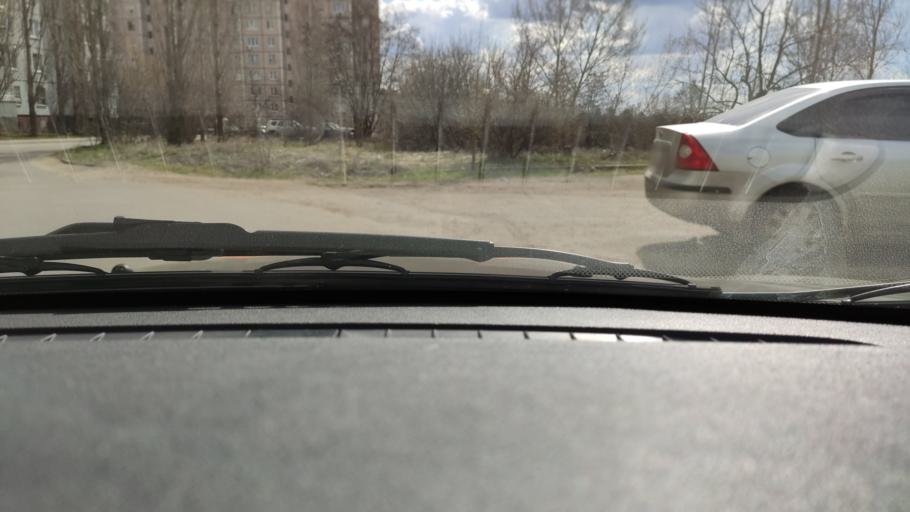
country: RU
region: Voronezj
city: Shilovo
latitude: 51.5591
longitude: 39.1138
